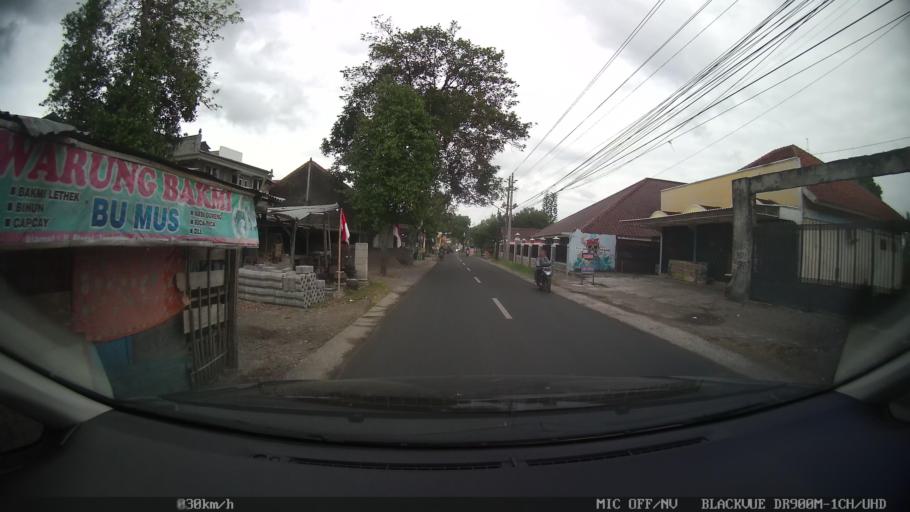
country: ID
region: Daerah Istimewa Yogyakarta
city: Sewon
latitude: -7.8570
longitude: 110.4094
